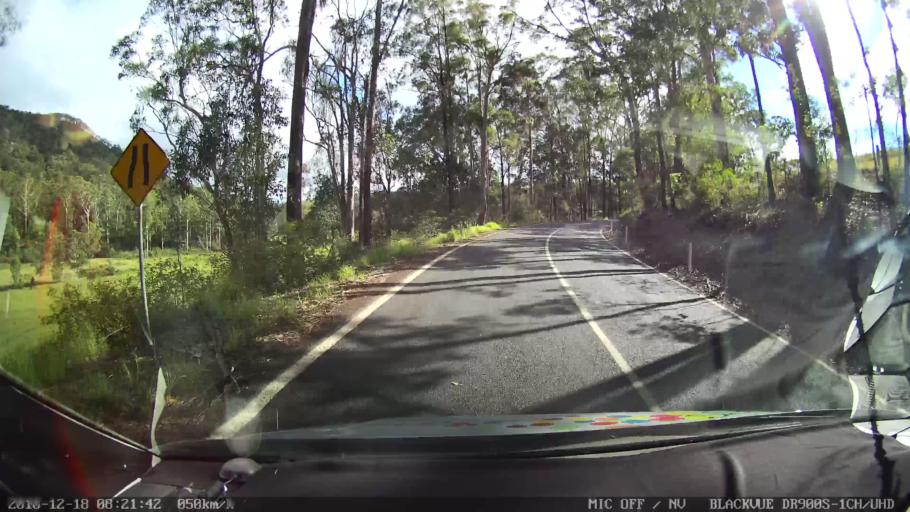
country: AU
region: New South Wales
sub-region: Kyogle
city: Kyogle
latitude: -28.3273
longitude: 152.7216
